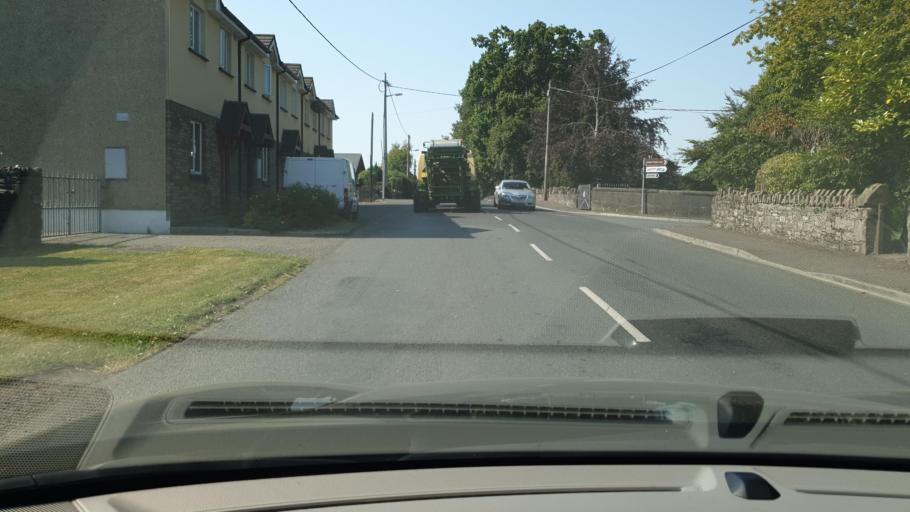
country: IE
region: Leinster
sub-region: An Mhi
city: Athboy
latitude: 53.6216
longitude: -6.9123
